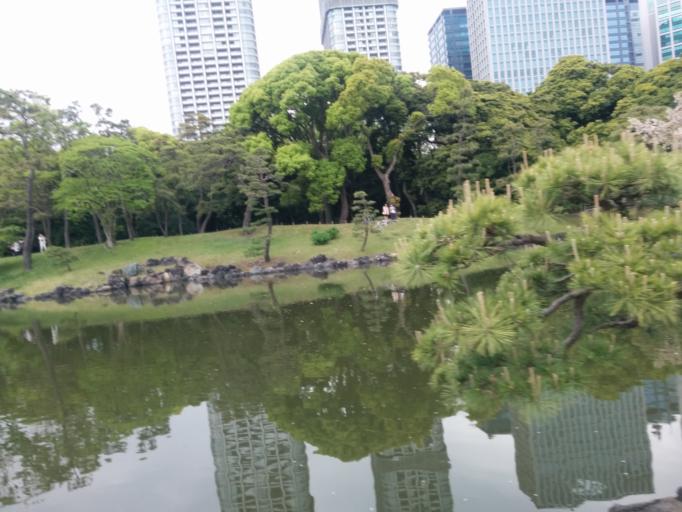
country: JP
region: Tokyo
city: Tokyo
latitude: 35.6591
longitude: 139.7626
